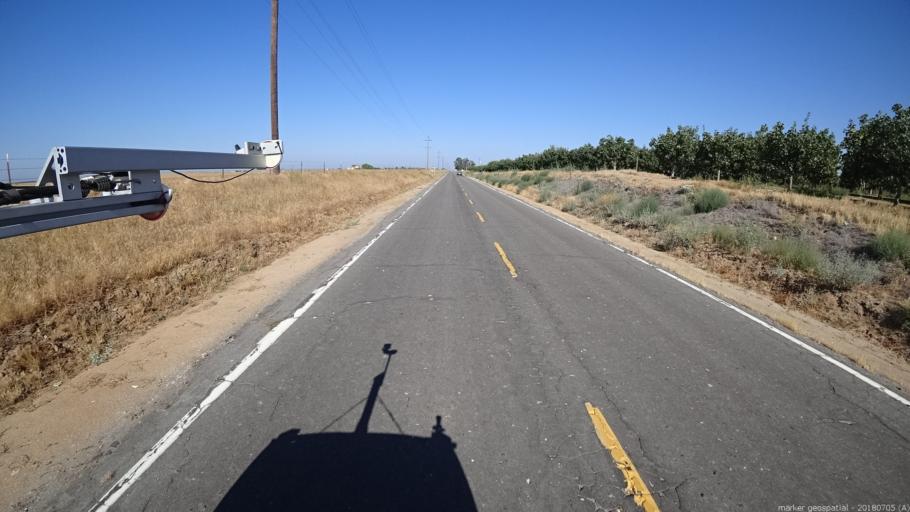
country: US
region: California
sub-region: Madera County
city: Madera Acres
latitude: 37.1267
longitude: -120.0535
